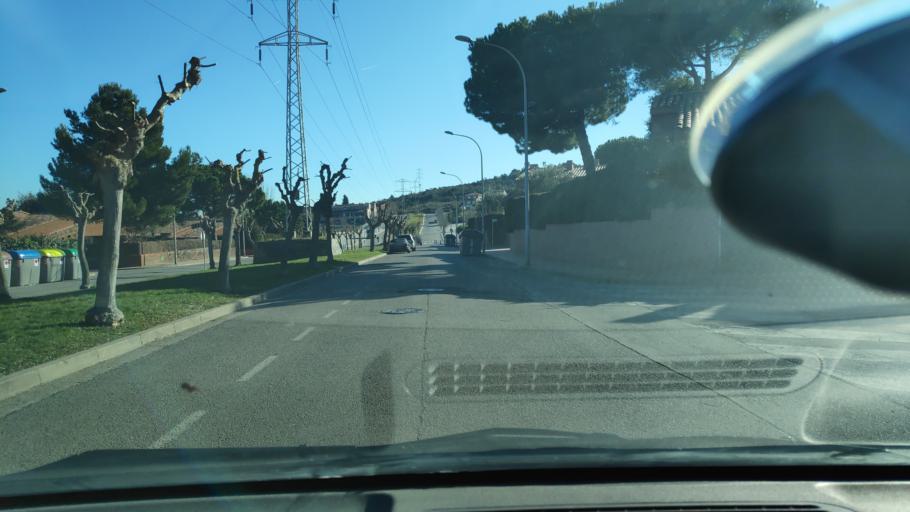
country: ES
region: Catalonia
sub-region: Provincia de Barcelona
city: Sant Quirze del Valles
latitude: 41.5288
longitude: 2.0765
